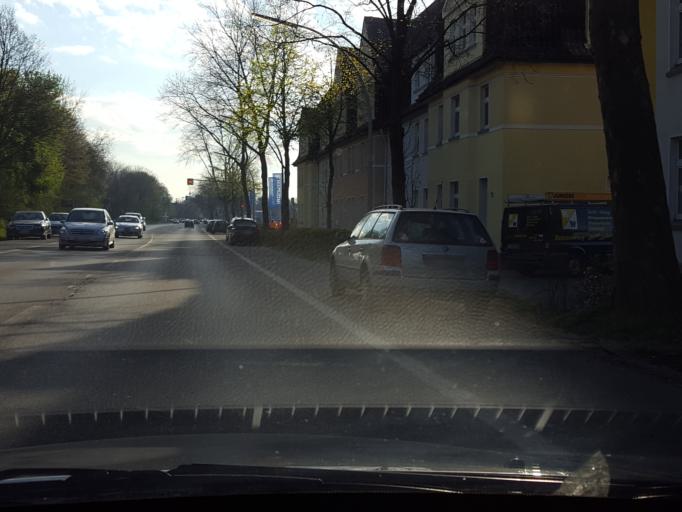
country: DE
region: North Rhine-Westphalia
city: Oer-Erkenschwick
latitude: 51.6501
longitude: 7.3226
